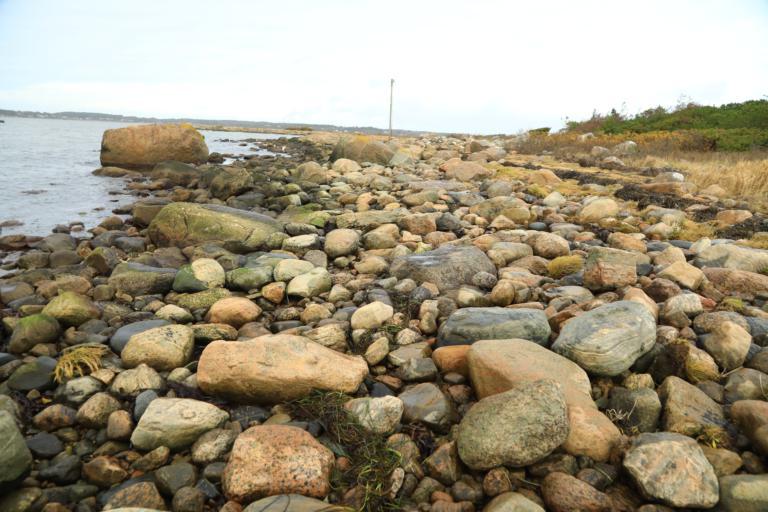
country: SE
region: Halland
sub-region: Varbergs Kommun
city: Varberg
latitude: 57.1724
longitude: 12.2026
